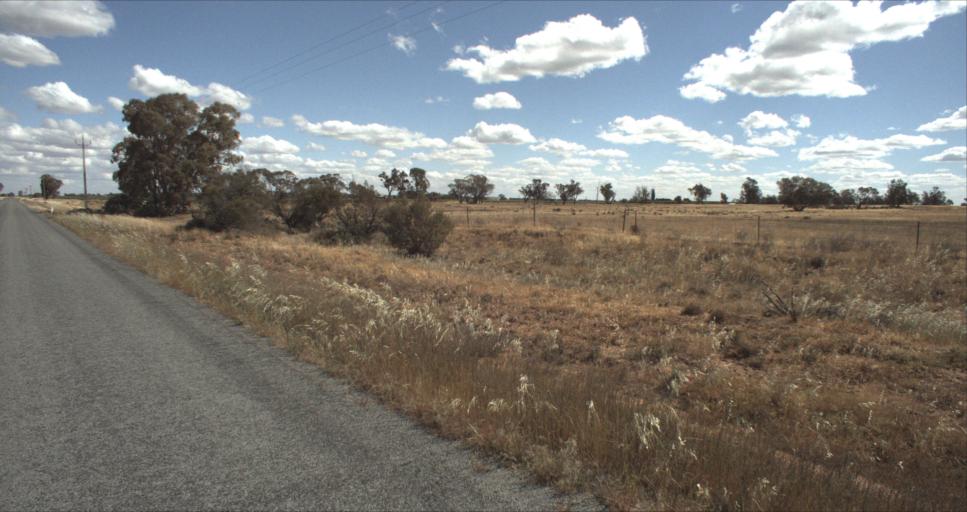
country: AU
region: New South Wales
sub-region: Leeton
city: Leeton
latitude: -34.4901
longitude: 146.2474
